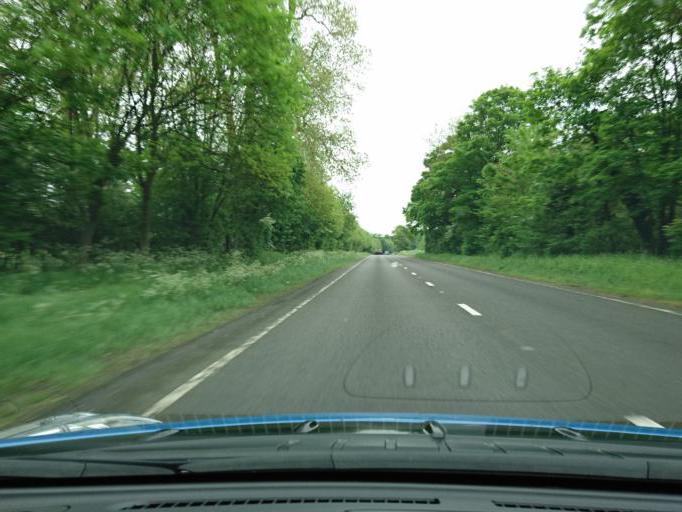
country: GB
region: England
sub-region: Oxfordshire
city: Wheatley
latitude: 51.7594
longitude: -1.1545
